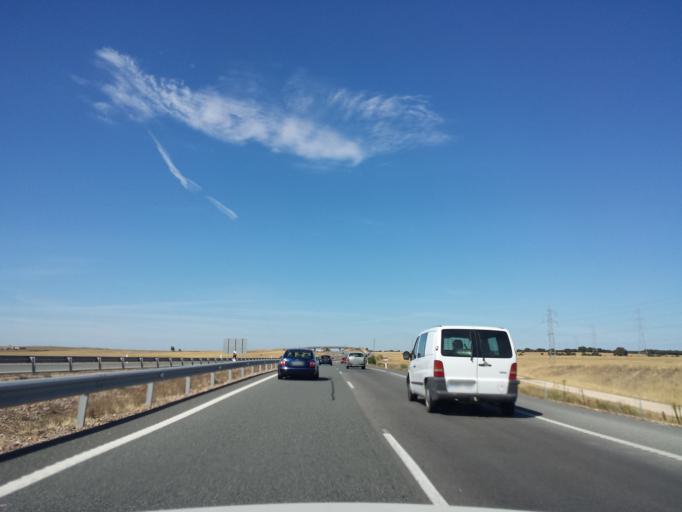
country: ES
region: Castille-La Mancha
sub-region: Province of Toledo
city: Velada
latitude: 39.9343
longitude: -4.9931
